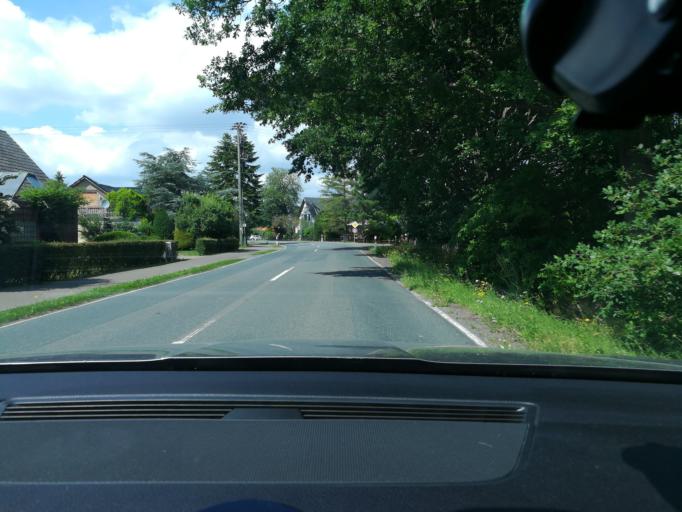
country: DE
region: North Rhine-Westphalia
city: Espelkamp
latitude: 52.3610
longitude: 8.6783
